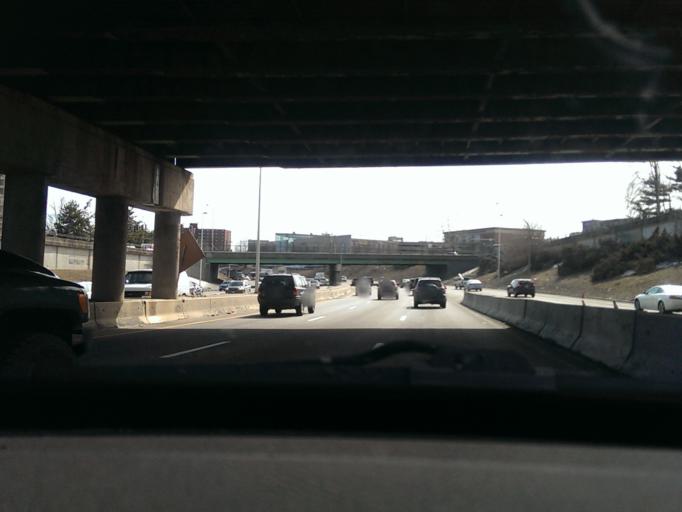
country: US
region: Rhode Island
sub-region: Providence County
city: Providence
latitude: 41.8233
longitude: -71.4201
